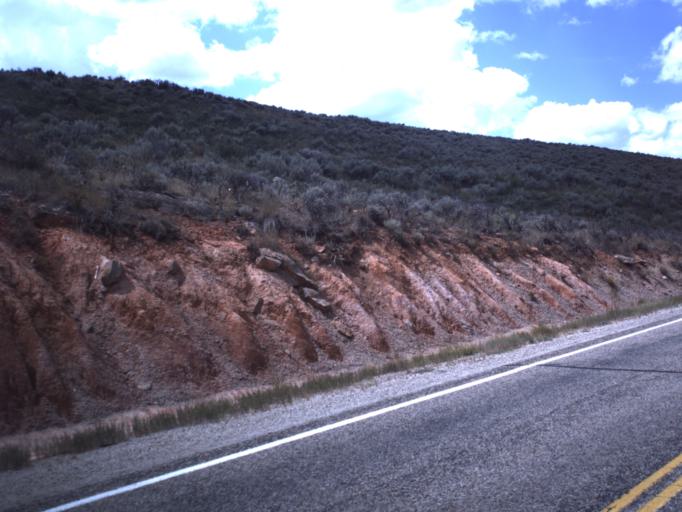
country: US
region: Utah
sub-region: Rich County
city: Randolph
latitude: 41.7821
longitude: -111.2015
